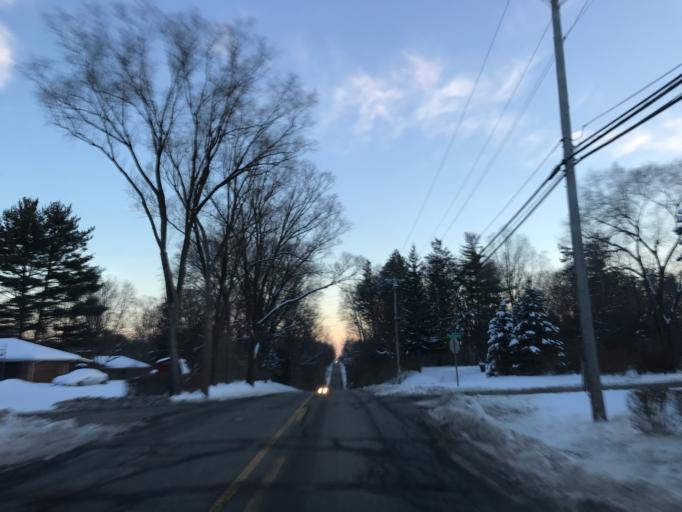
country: US
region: Michigan
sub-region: Oakland County
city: Bingham Farms
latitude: 42.4698
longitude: -83.2987
